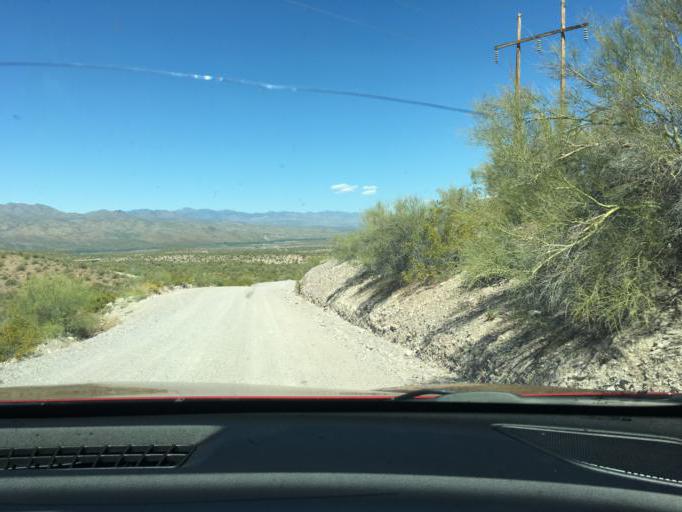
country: US
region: Arizona
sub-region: Yavapai County
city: Bagdad
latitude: 34.6093
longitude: -113.5113
